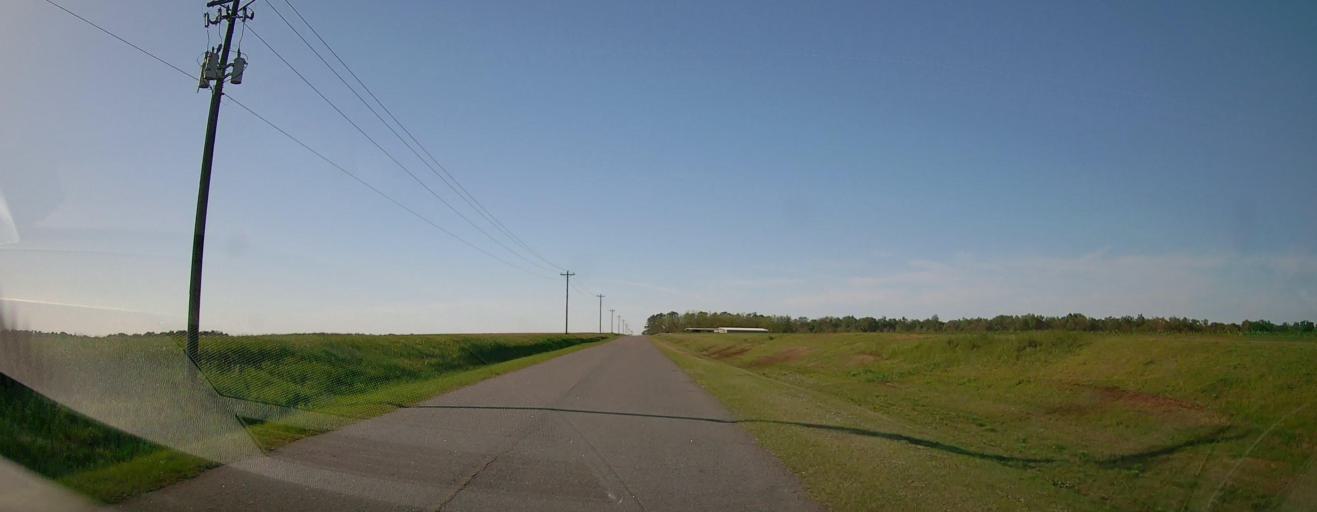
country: US
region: Georgia
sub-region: Houston County
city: Perry
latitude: 32.4234
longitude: -83.7780
